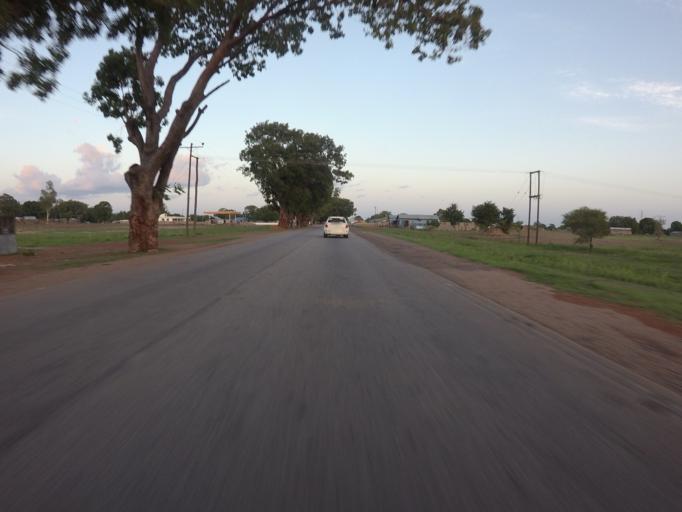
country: GH
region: Upper East
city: Navrongo
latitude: 10.8569
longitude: -1.0269
